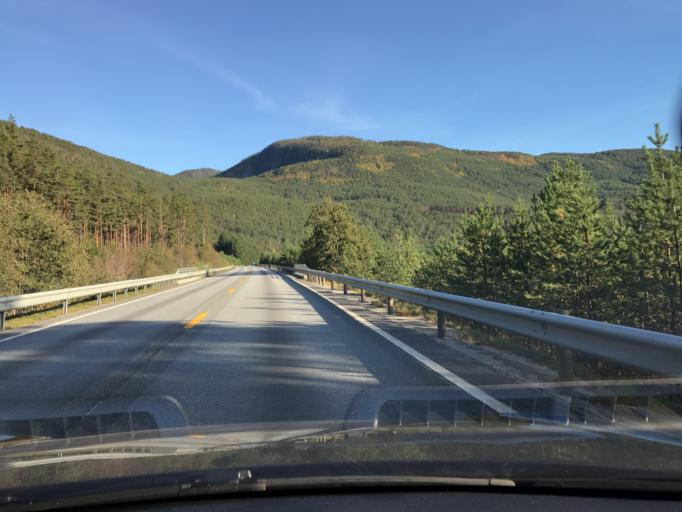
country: NO
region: Sogn og Fjordane
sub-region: Sogndal
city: Sogndalsfjora
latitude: 61.1816
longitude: 7.2843
